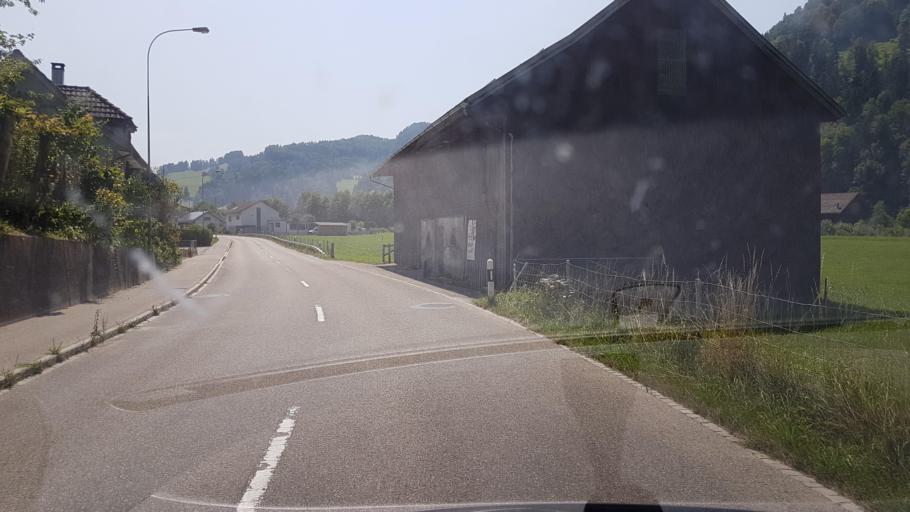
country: CH
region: Saint Gallen
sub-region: Wahlkreis Toggenburg
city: Mogelsberg
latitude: 47.3451
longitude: 9.1296
